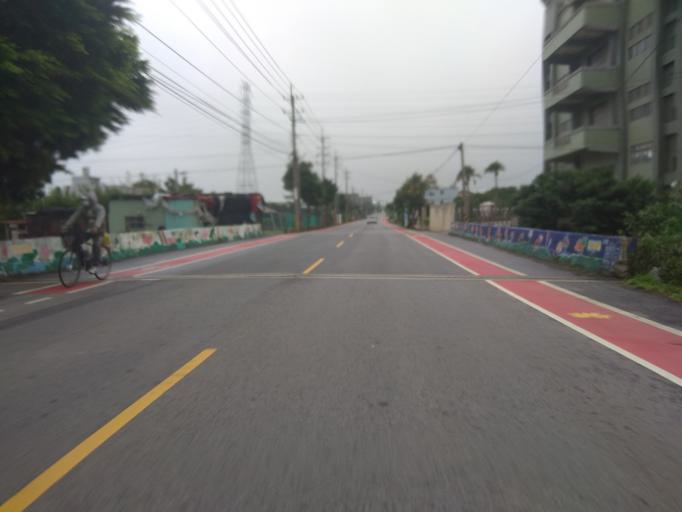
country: TW
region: Taiwan
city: Taoyuan City
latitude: 25.0021
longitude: 121.1251
